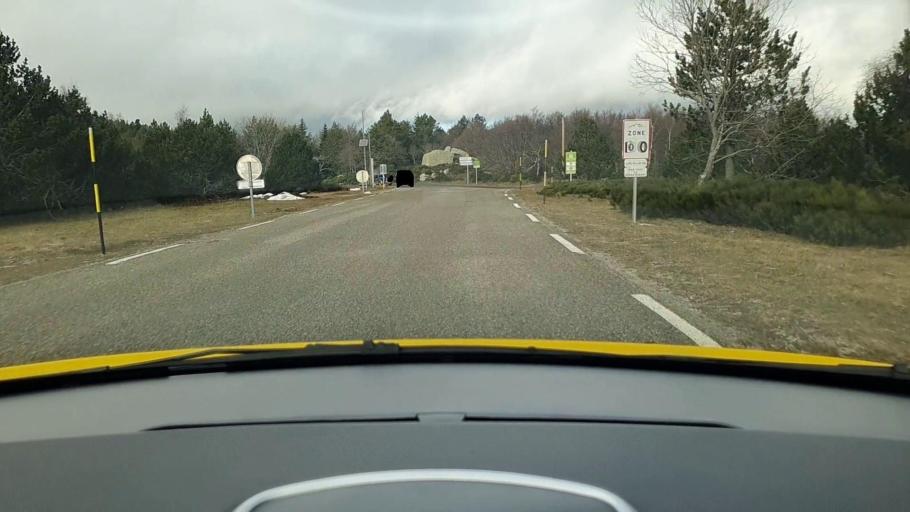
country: FR
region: Languedoc-Roussillon
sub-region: Departement du Gard
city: Branoux-les-Taillades
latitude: 44.3914
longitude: 3.8932
